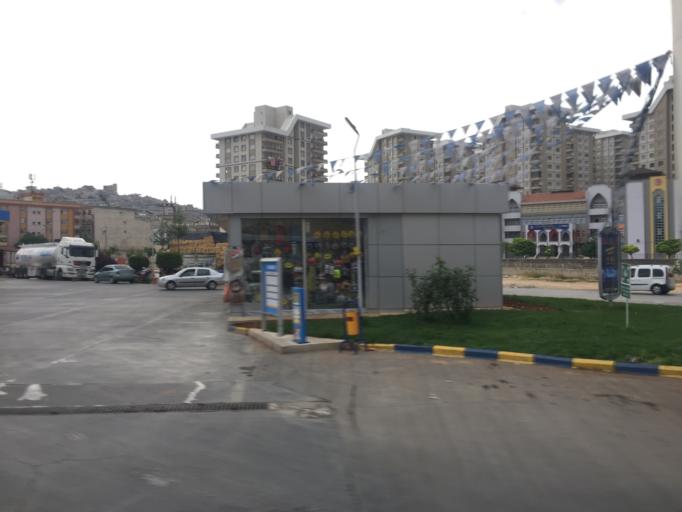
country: TR
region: Gaziantep
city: Gaziantep
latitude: 37.0740
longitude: 37.4127
